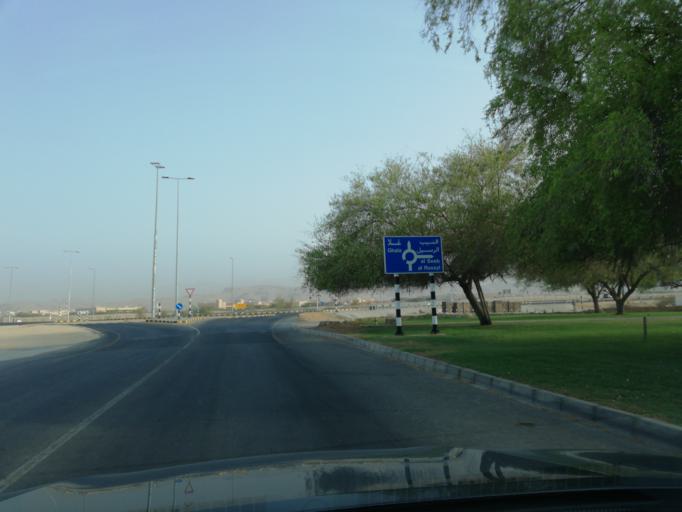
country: OM
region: Muhafazat Masqat
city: As Sib al Jadidah
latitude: 23.5823
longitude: 58.2711
